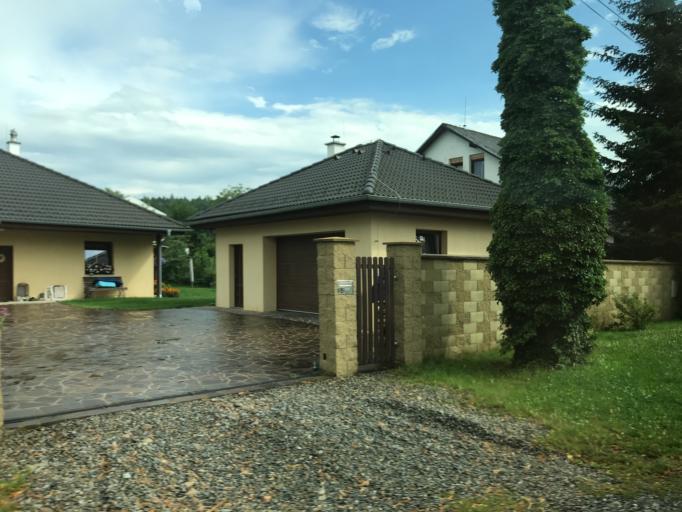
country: CZ
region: Jihocesky
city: Vcelna
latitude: 48.9295
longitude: 14.4576
